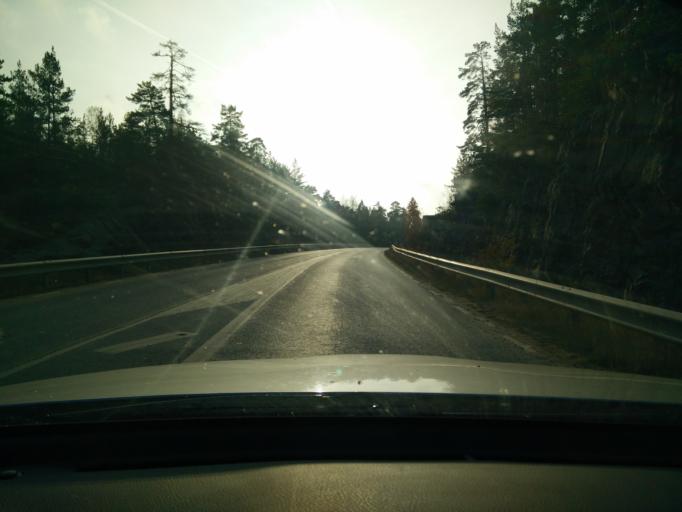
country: SE
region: Stockholm
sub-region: Sollentuna Kommun
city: Sollentuna
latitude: 59.4639
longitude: 17.9800
